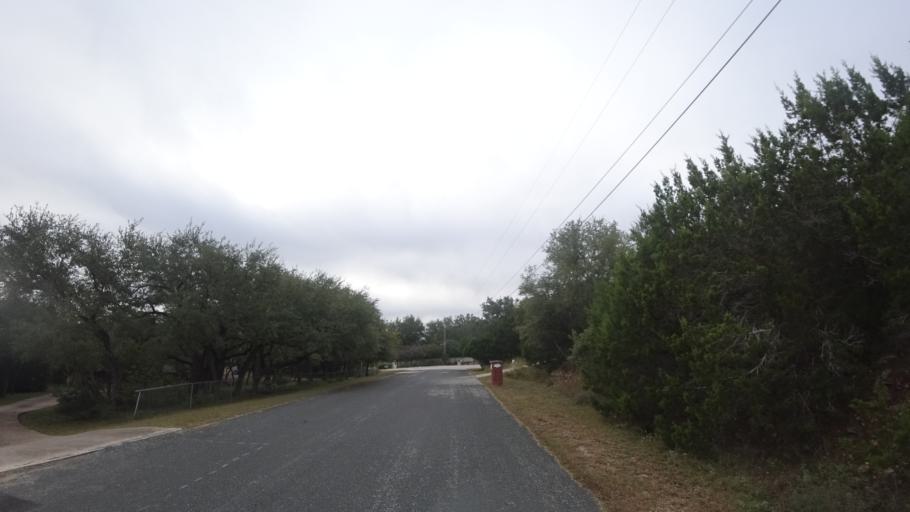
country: US
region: Texas
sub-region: Travis County
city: Hudson Bend
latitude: 30.3862
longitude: -97.9172
